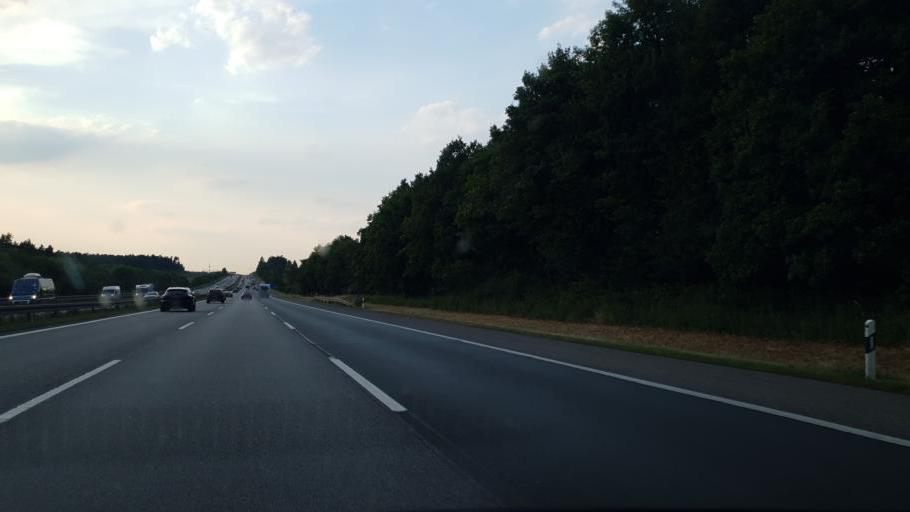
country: DE
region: Bavaria
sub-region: Regierungsbezirk Mittelfranken
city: Hilpoltstein
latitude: 49.1886
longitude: 11.2505
